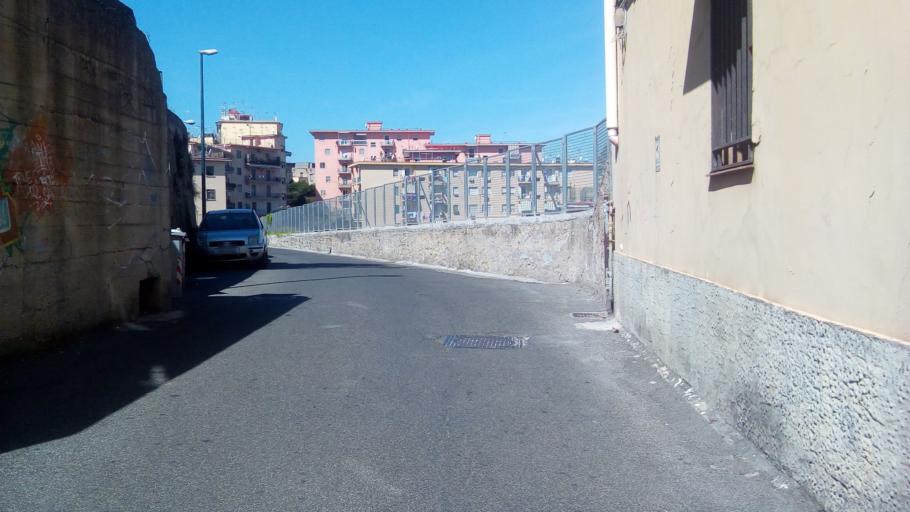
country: IT
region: Campania
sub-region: Provincia di Napoli
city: Napoli
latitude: 40.8647
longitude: 14.2566
